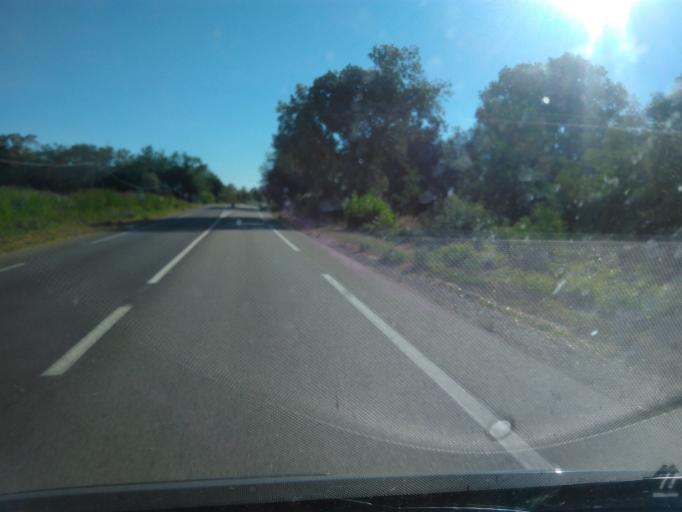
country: FR
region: Languedoc-Roussillon
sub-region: Departement du Gard
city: Saint-Gilles
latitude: 43.6711
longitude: 4.4782
